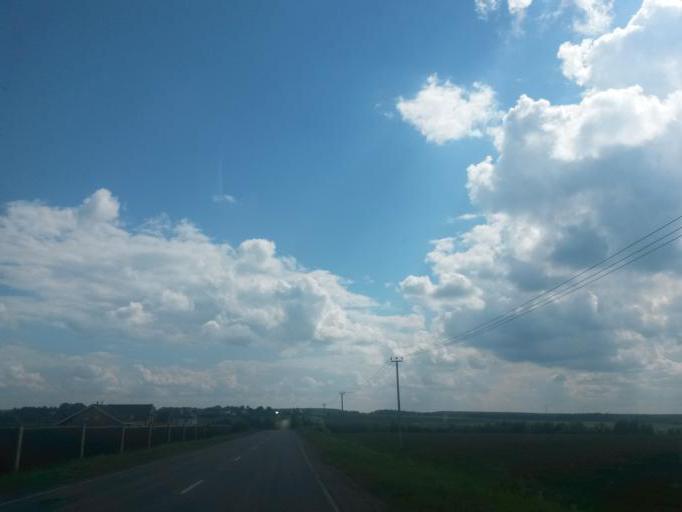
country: RU
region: Moskovskaya
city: Barybino
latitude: 55.2392
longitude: 37.7969
